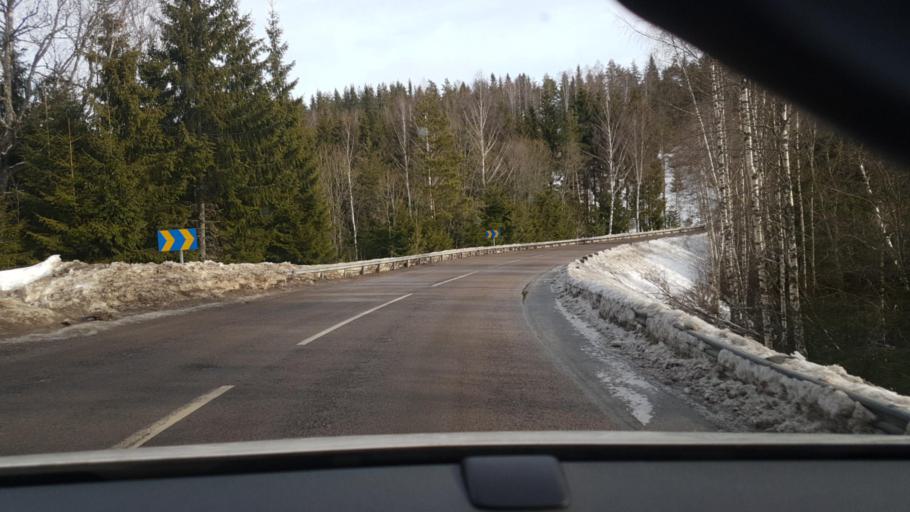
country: SE
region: Vaermland
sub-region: Arjangs Kommun
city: Arjaeng
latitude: 59.5619
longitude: 12.1746
